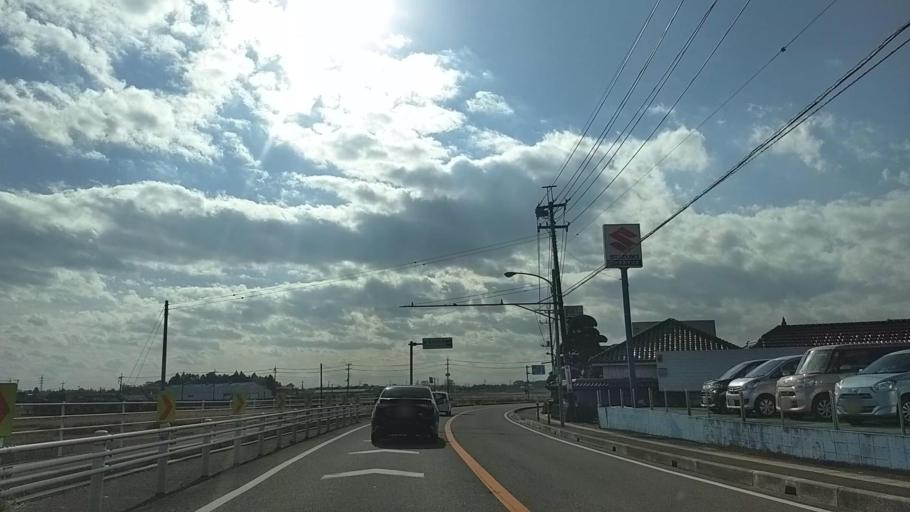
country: JP
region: Chiba
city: Naruto
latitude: 35.6318
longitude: 140.4501
